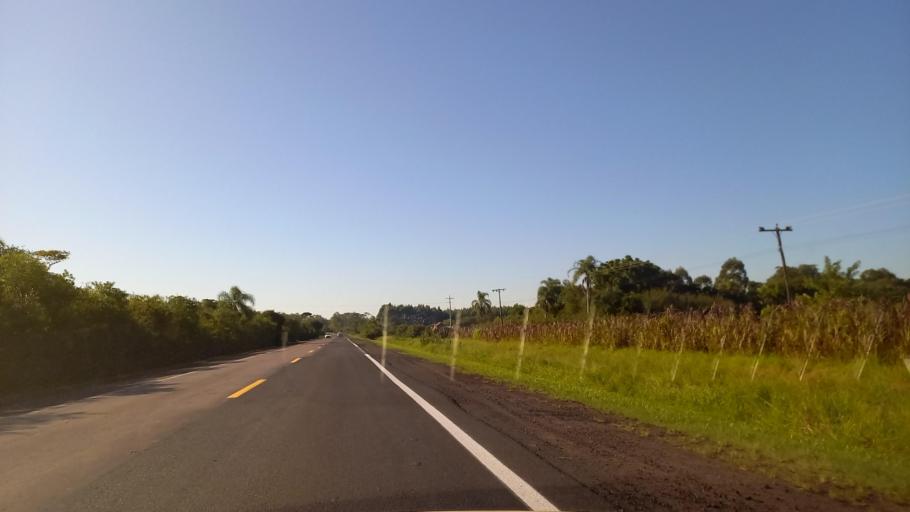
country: BR
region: Rio Grande do Sul
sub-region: Venancio Aires
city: Venancio Aires
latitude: -29.6678
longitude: -52.0438
